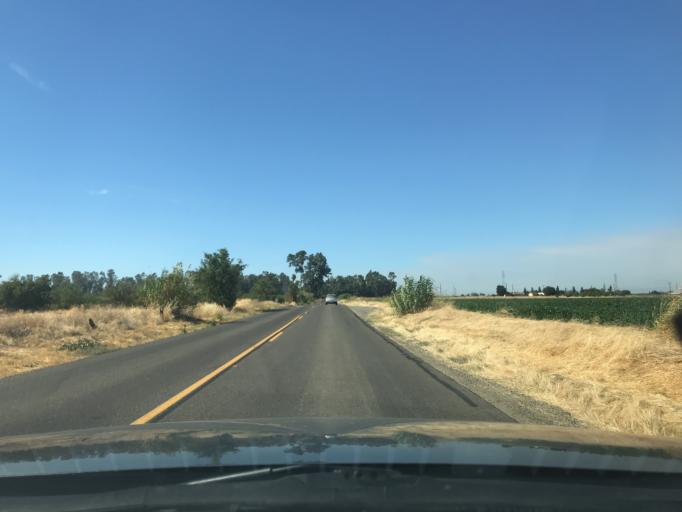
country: US
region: California
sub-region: Merced County
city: Atwater
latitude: 37.3433
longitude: -120.5587
